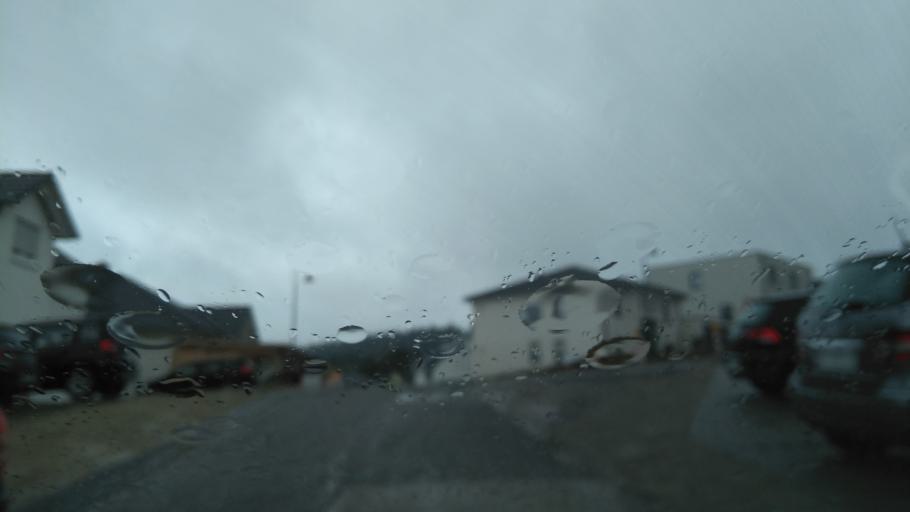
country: DE
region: Rheinland-Pfalz
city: Pellingen
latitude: 49.6784
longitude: 6.6688
